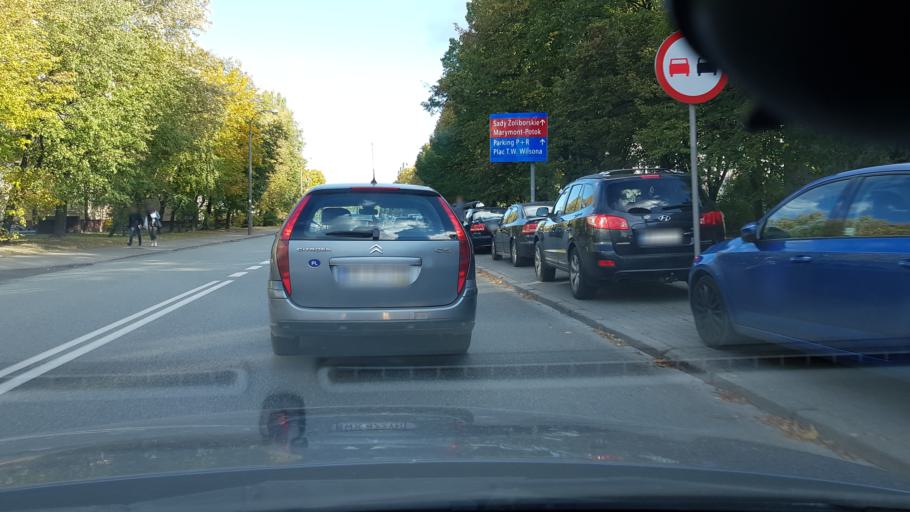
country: PL
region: Masovian Voivodeship
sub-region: Warszawa
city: Bielany
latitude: 52.2762
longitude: 20.9545
